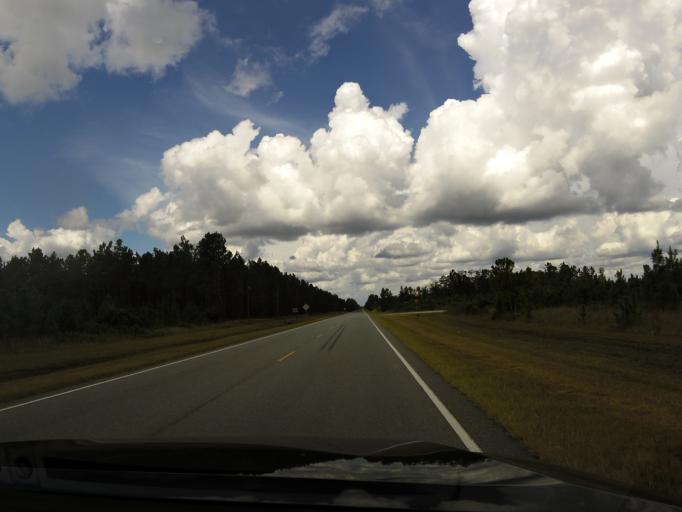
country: US
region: Georgia
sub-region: Charlton County
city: Folkston
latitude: 30.8964
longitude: -82.0167
